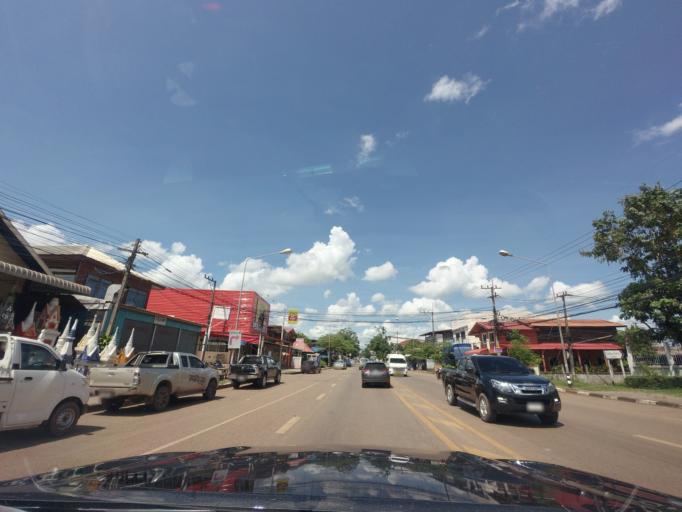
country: TH
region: Changwat Udon Thani
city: Ban Dung
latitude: 17.6929
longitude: 103.2579
